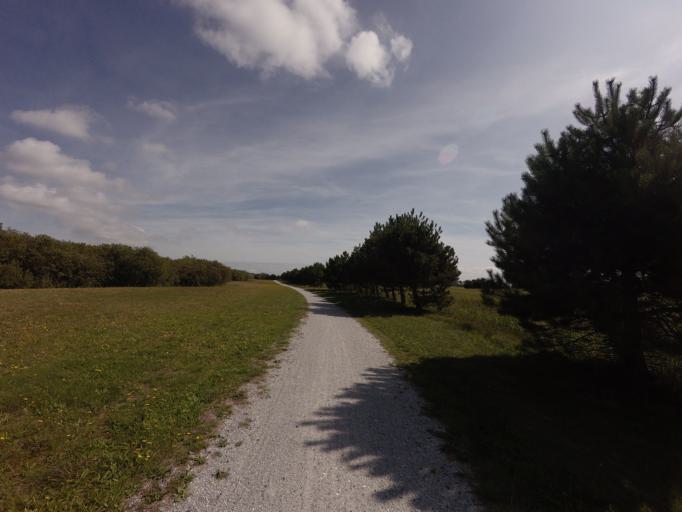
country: NL
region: Friesland
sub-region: Gemeente Ameland
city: Hollum
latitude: 53.4483
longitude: 5.6479
